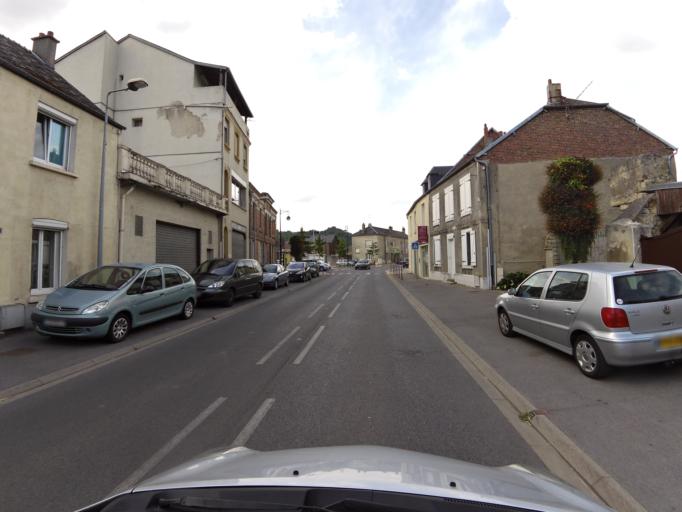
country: FR
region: Picardie
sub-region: Departement de l'Aisne
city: Laon
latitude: 49.5483
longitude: 3.6300
